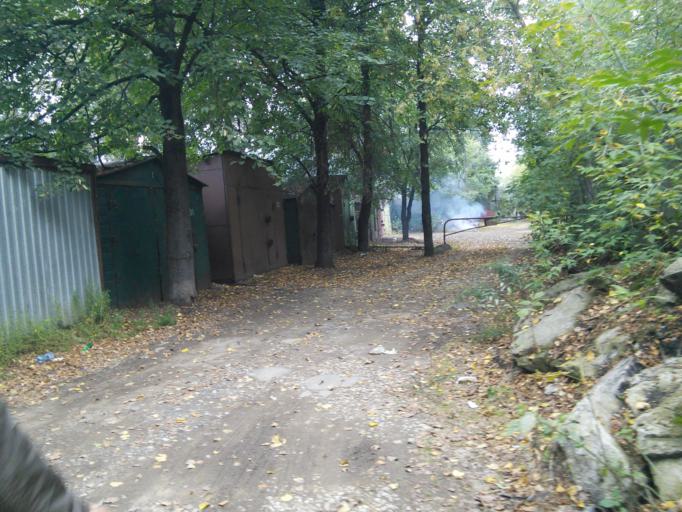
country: RU
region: Moskovskaya
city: Kozhukhovo
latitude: 55.7136
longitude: 37.6855
